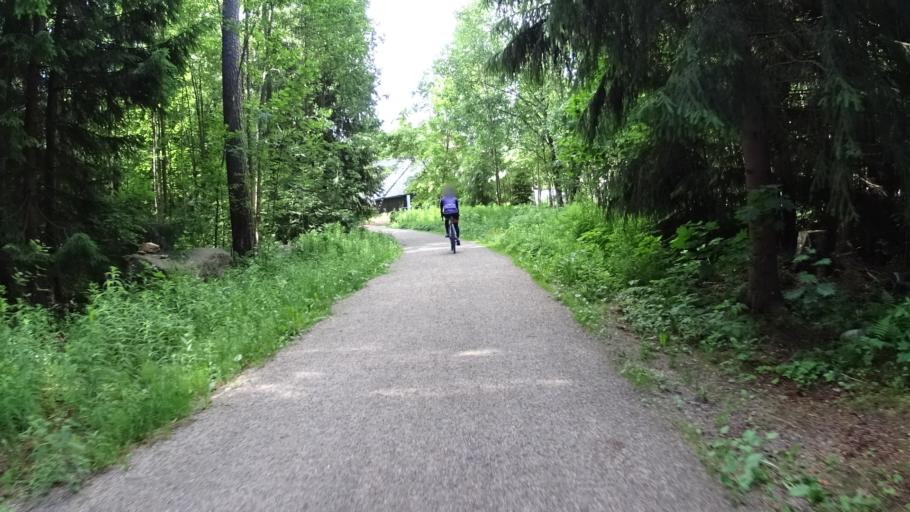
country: FI
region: Uusimaa
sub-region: Helsinki
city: Kilo
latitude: 60.1909
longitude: 24.7902
